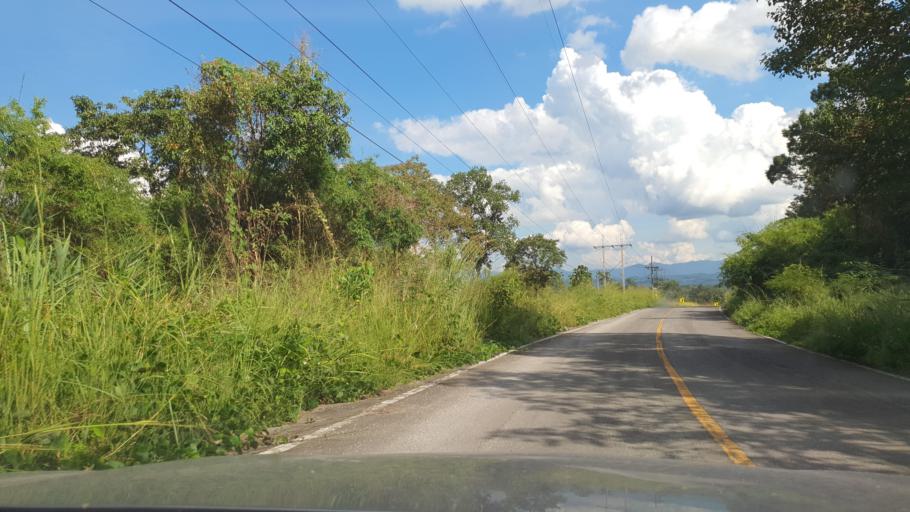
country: TH
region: Chiang Rai
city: Wiang Pa Pao
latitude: 19.3311
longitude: 99.4641
